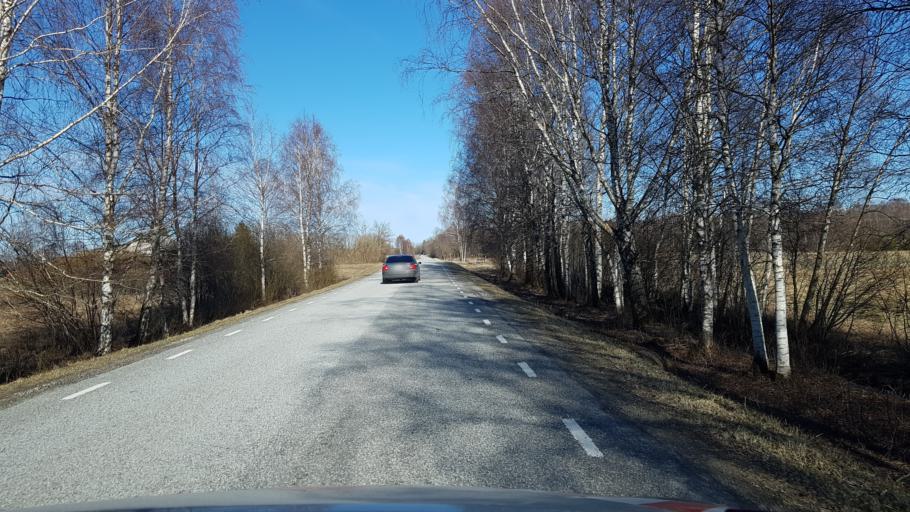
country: EE
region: Laeaene-Virumaa
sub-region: Kadrina vald
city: Kadrina
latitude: 59.3450
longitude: 26.0901
